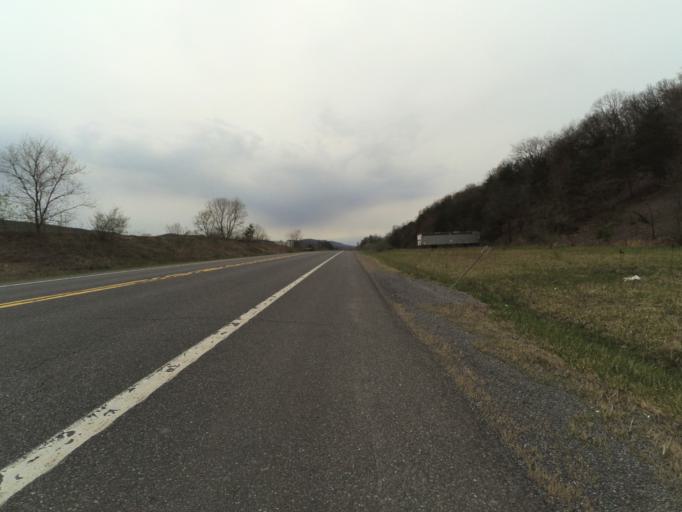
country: US
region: Pennsylvania
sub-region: Centre County
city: Milesburg
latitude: 40.9839
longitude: -77.7246
